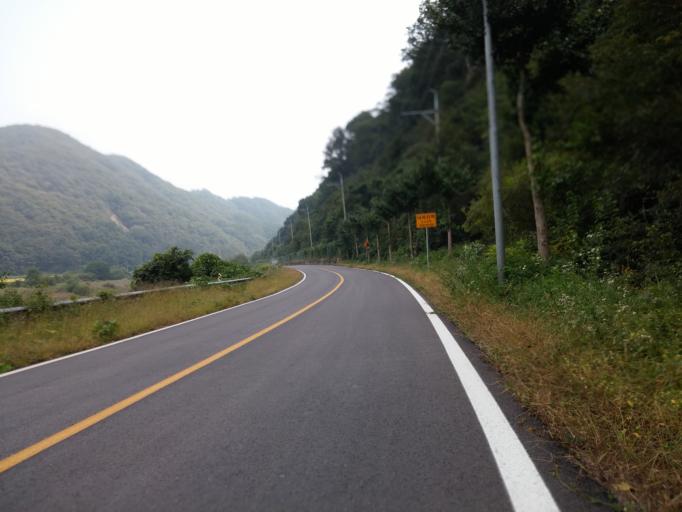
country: KR
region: Chungcheongbuk-do
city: Yong-dong
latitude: 36.3970
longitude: 127.8046
